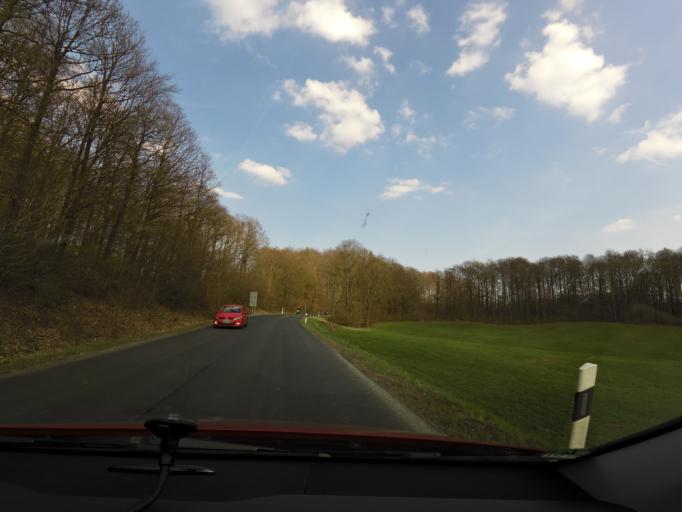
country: DE
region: Lower Saxony
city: Waake
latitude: 51.5969
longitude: 10.0388
